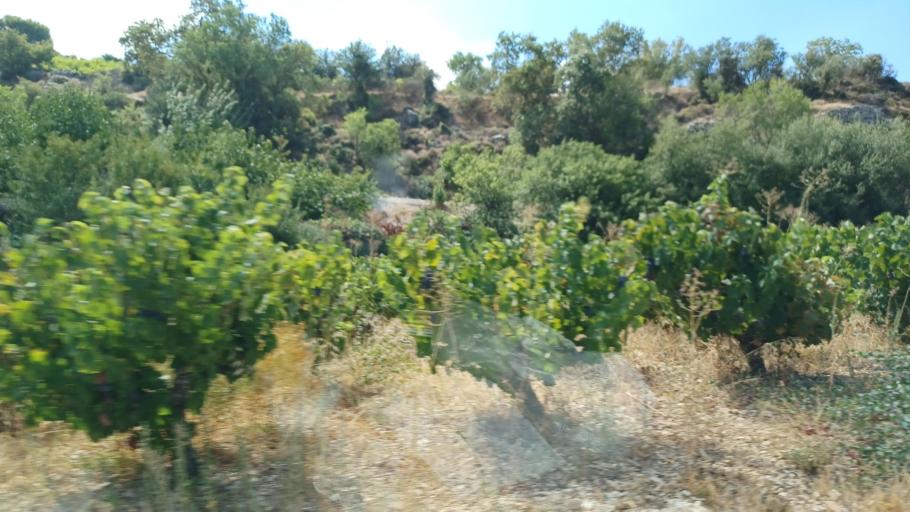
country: CY
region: Pafos
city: Mesogi
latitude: 34.8810
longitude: 32.6106
